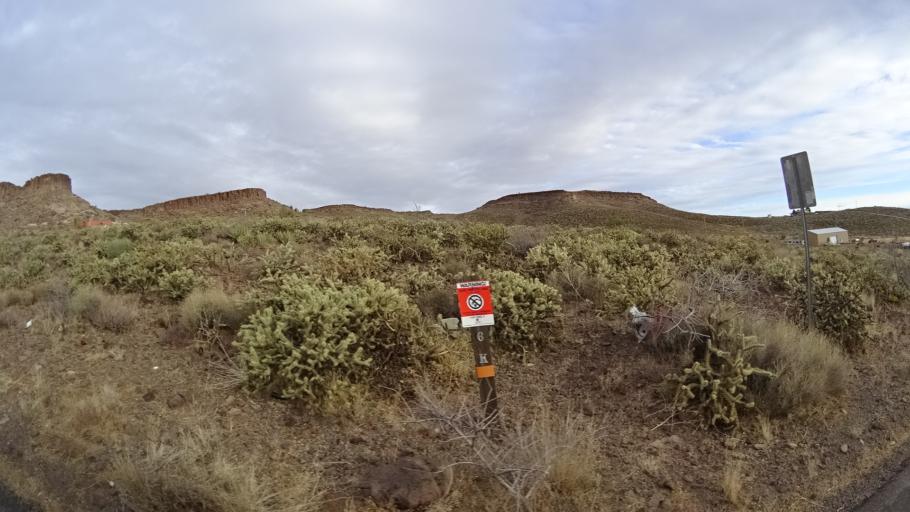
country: US
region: Arizona
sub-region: Mohave County
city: Kingman
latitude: 35.2178
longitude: -114.0590
